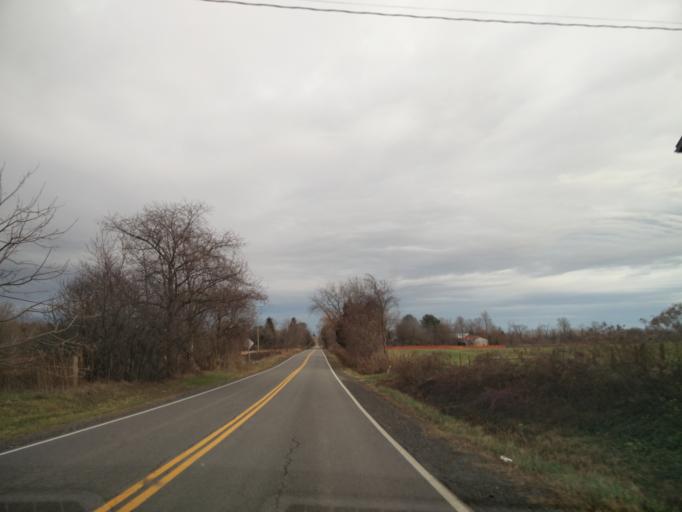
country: US
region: New York
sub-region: Tompkins County
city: Trumansburg
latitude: 42.5364
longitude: -76.6934
